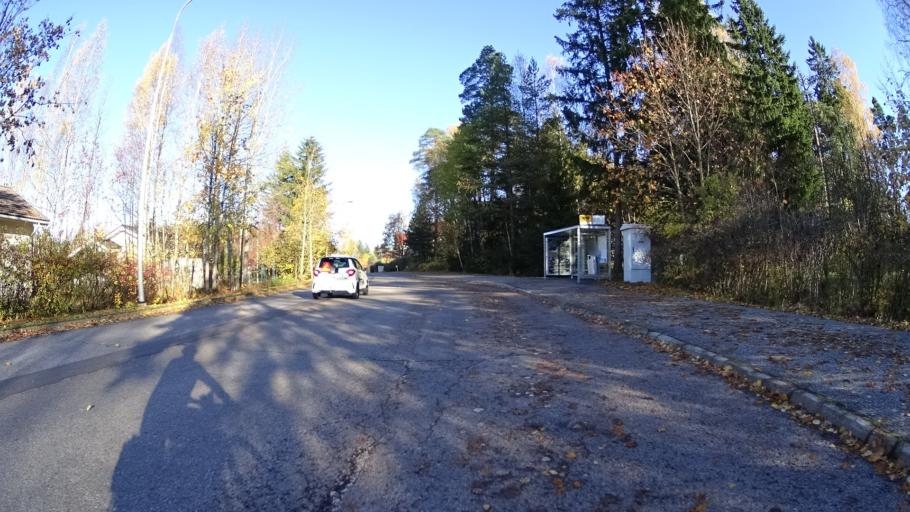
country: FI
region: Uusimaa
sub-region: Helsinki
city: Kilo
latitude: 60.2816
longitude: 24.7852
